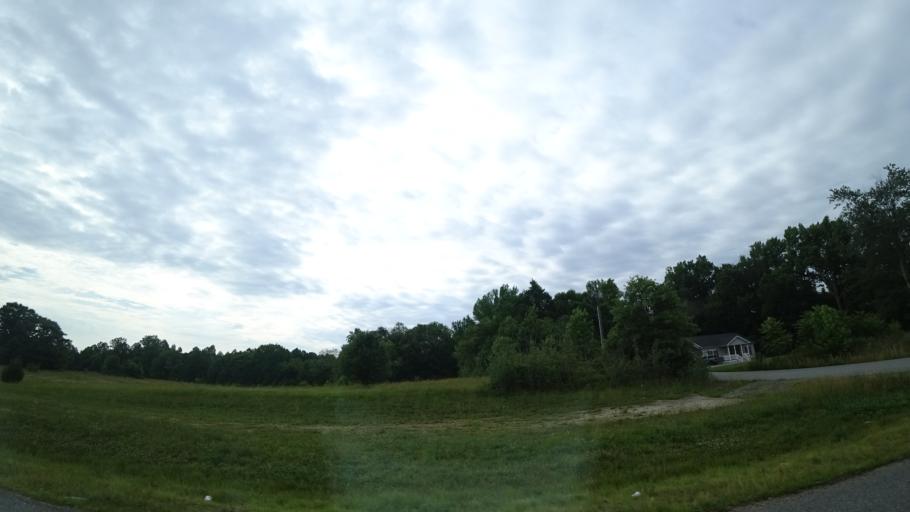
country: US
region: Virginia
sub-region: Spotsylvania County
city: Spotsylvania Courthouse
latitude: 38.1739
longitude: -77.6326
